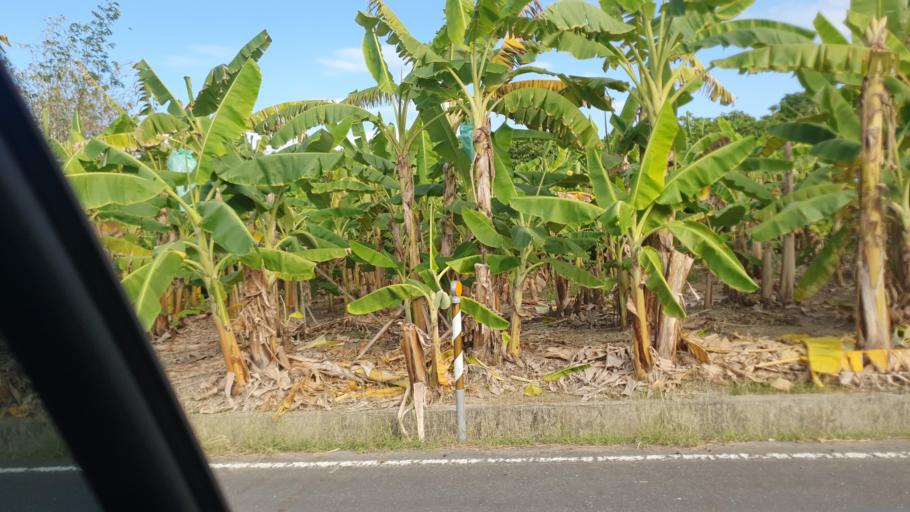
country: TW
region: Taiwan
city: Yujing
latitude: 23.0451
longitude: 120.4222
